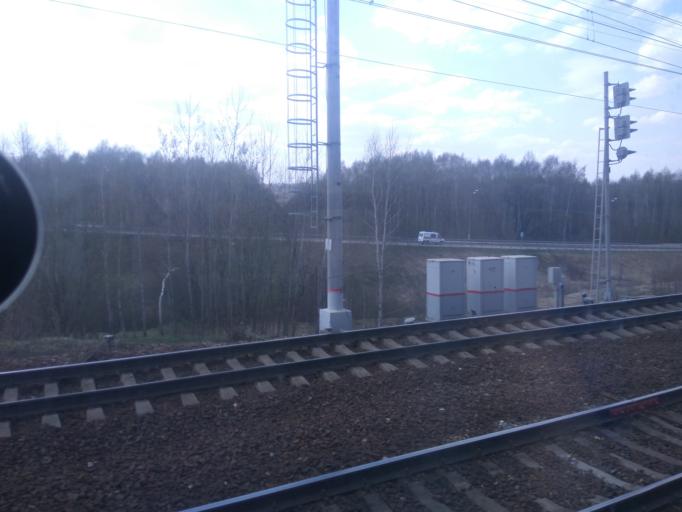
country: RU
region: Moskovskaya
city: Yakhroma
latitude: 56.2966
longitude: 37.4967
